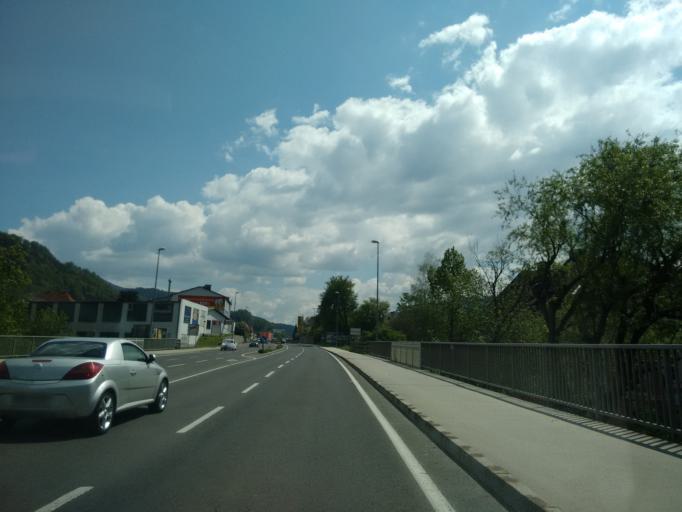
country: AT
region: Styria
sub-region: Politischer Bezirk Bruck-Muerzzuschlag
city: Bruck an der Mur
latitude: 47.4279
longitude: 15.2686
